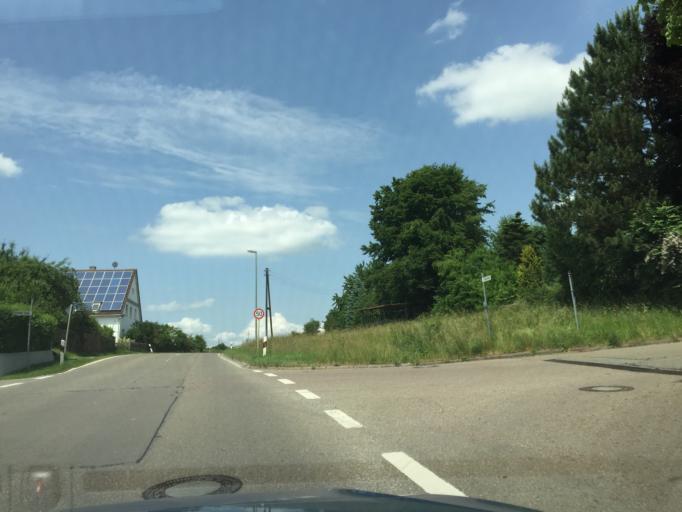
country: DE
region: Bavaria
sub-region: Swabia
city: Zusamaltheim
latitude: 48.5242
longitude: 10.6308
